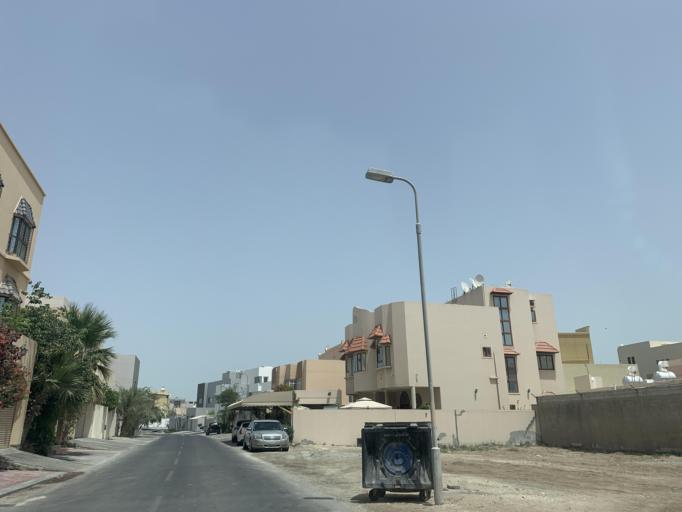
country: BH
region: Northern
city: Sitrah
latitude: 26.1455
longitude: 50.5877
